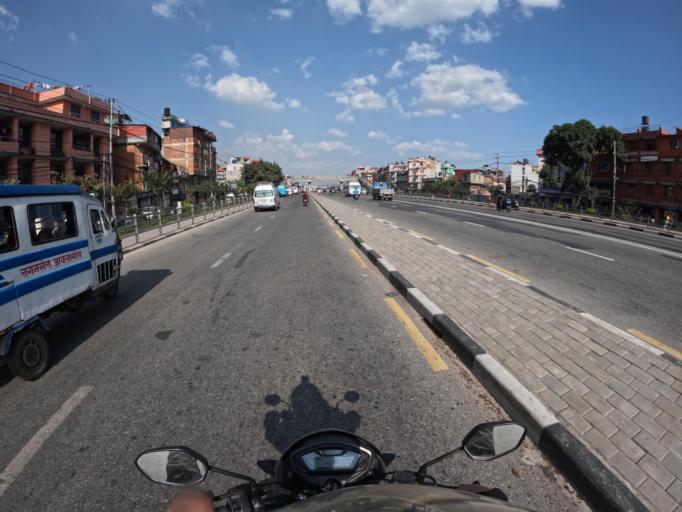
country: NP
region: Central Region
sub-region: Bagmati Zone
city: Patan
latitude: 27.6770
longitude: 85.3463
